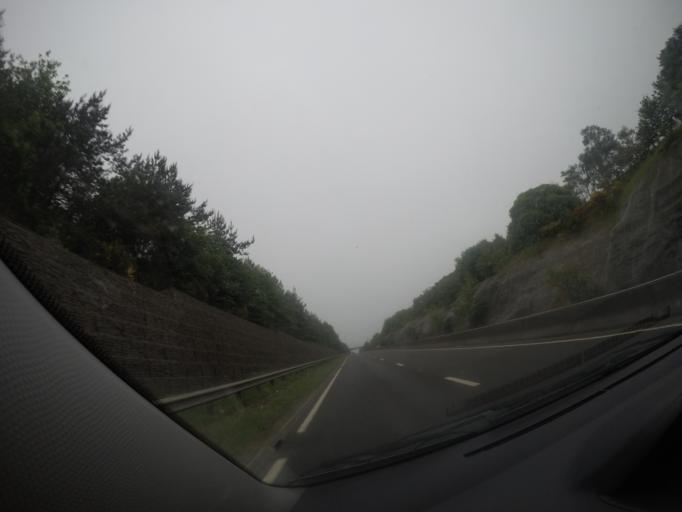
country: GB
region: Scotland
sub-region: Dundee City
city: Dundee
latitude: 56.5010
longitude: -2.9488
